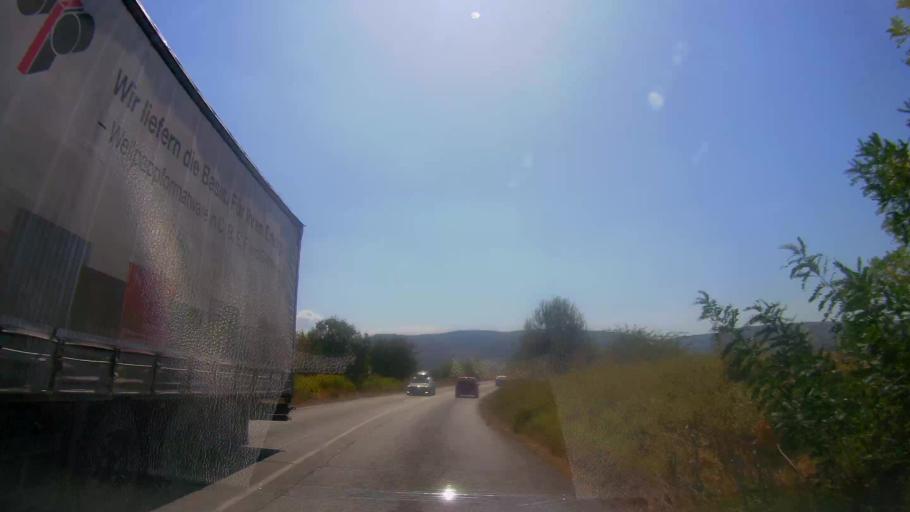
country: BG
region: Veliko Turnovo
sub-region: Obshtina Gorna Oryakhovitsa
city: Purvomaytsi
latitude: 43.1622
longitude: 25.6193
